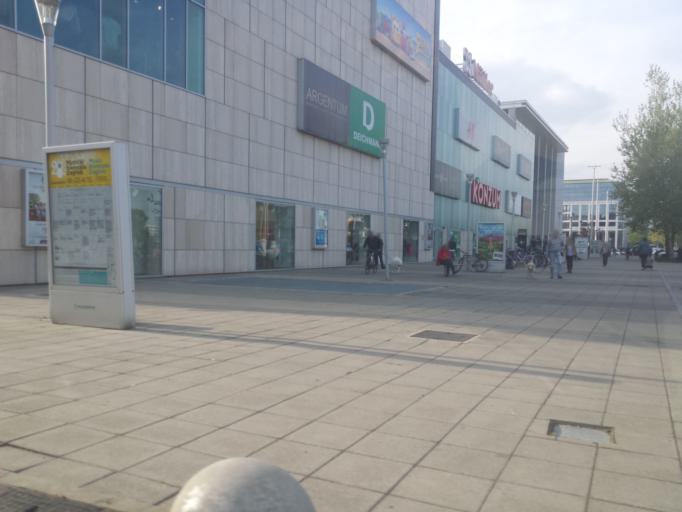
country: HR
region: Grad Zagreb
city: Novi Zagreb
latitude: 45.7758
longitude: 15.9796
